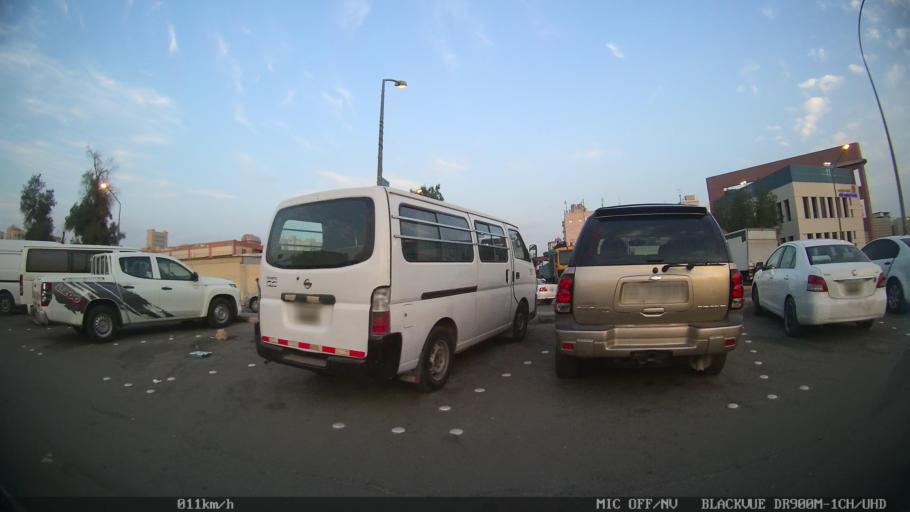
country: KW
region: Al Farwaniyah
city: Al Farwaniyah
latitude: 29.2934
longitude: 47.9717
